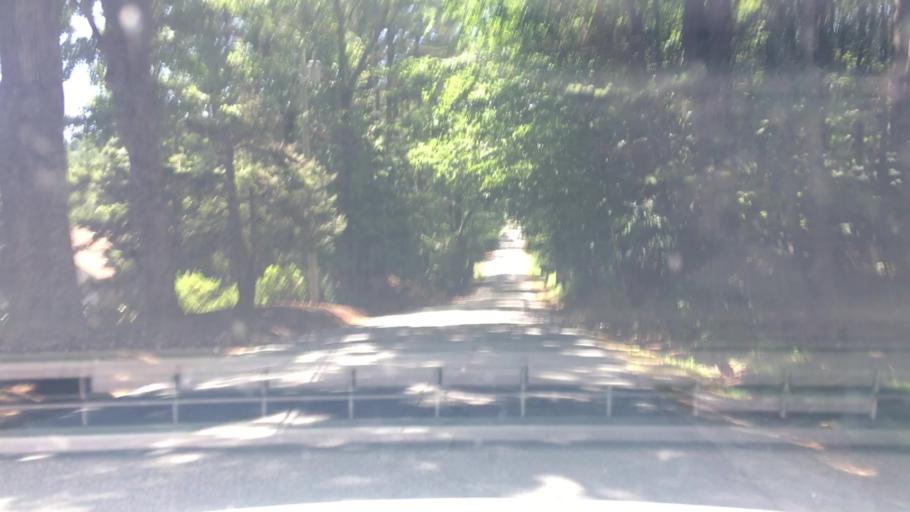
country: US
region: New Hampshire
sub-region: Merrimack County
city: Hopkinton
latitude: 43.2092
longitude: -71.6701
